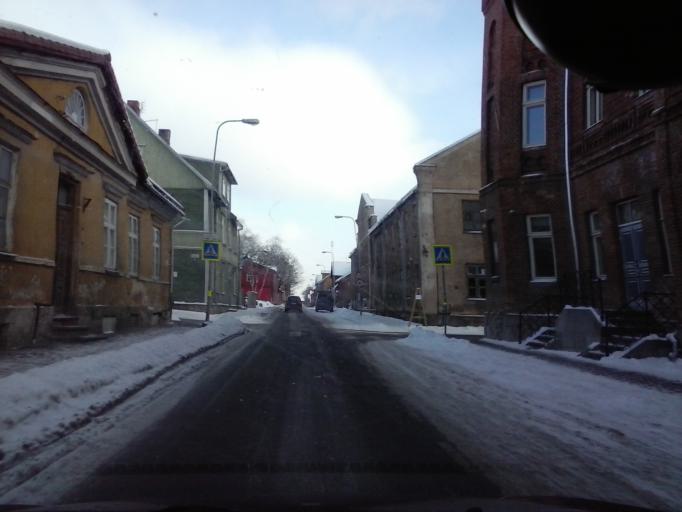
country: EE
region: Viljandimaa
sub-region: Viljandi linn
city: Viljandi
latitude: 58.3664
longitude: 25.6033
